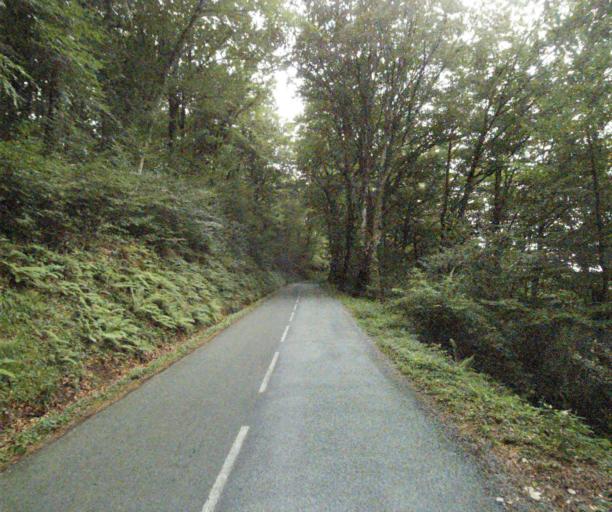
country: FR
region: Midi-Pyrenees
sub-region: Departement du Tarn
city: Soreze
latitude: 43.4363
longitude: 2.0901
